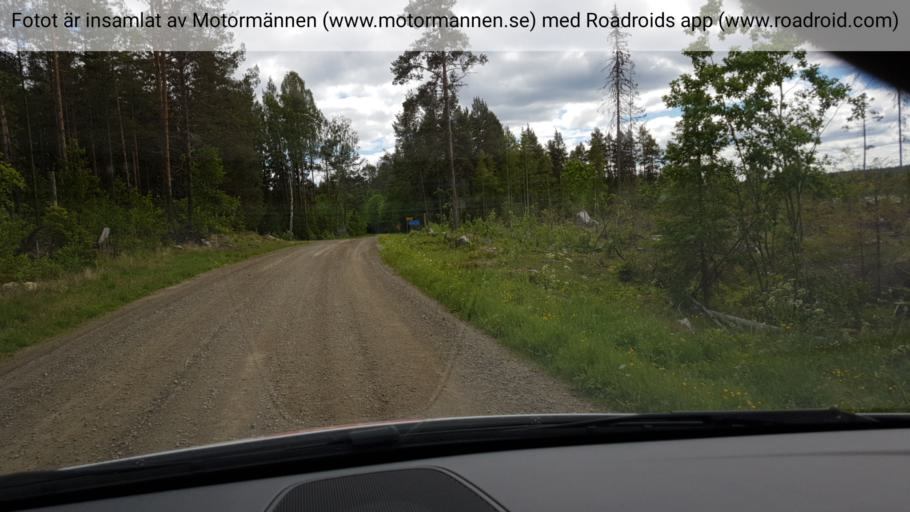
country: SE
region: Jaemtland
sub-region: Braecke Kommun
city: Braecke
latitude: 62.7959
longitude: 15.2647
